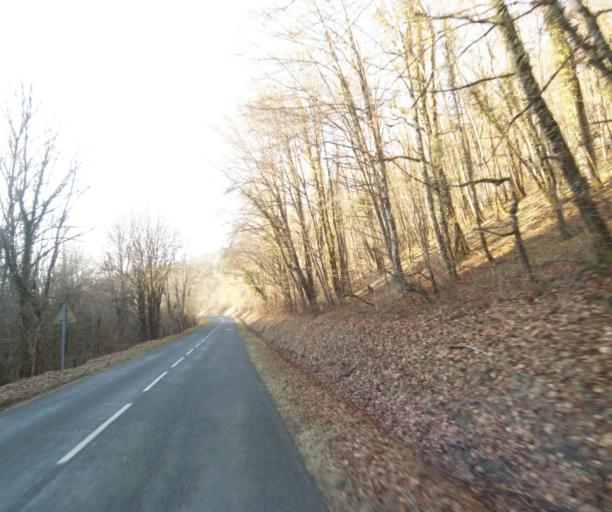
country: FR
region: Champagne-Ardenne
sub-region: Departement de la Haute-Marne
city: Chevillon
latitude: 48.5288
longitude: 5.1785
